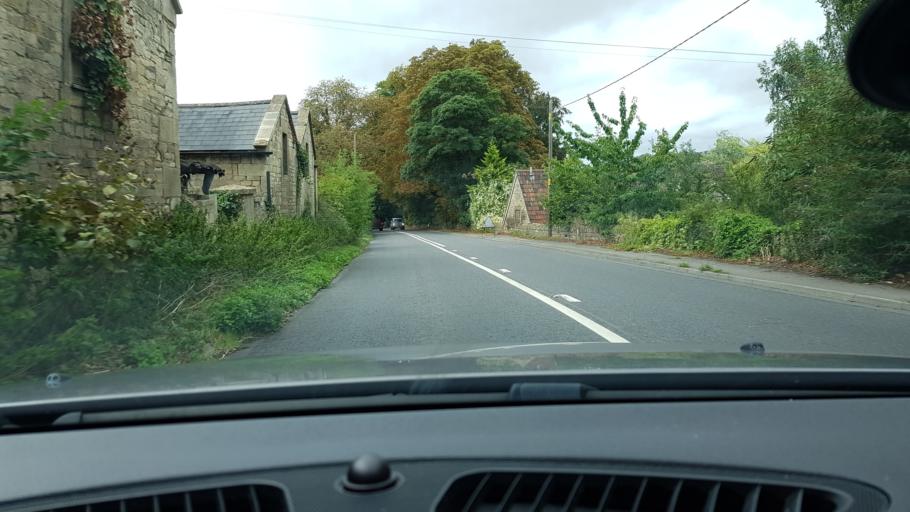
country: GB
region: England
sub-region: Wiltshire
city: Box
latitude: 51.4233
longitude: -2.2433
